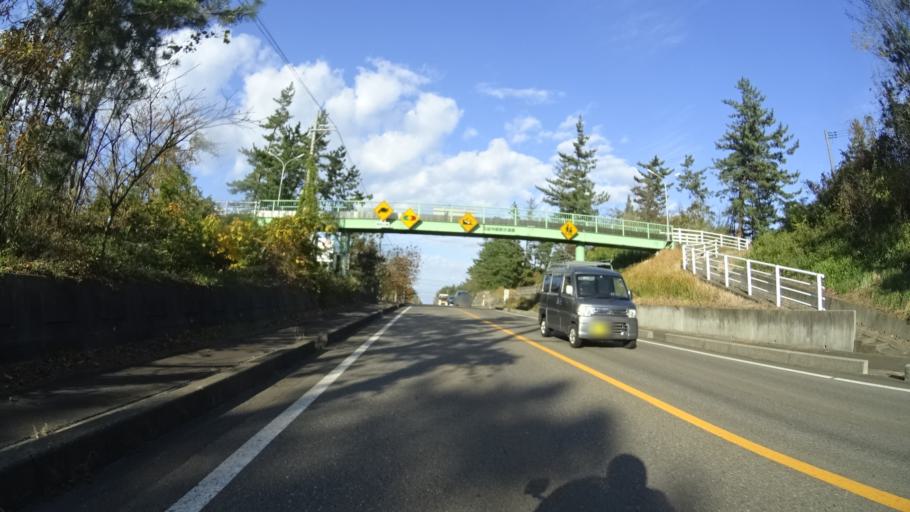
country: JP
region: Niigata
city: Kashiwazaki
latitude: 37.2824
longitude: 138.3983
